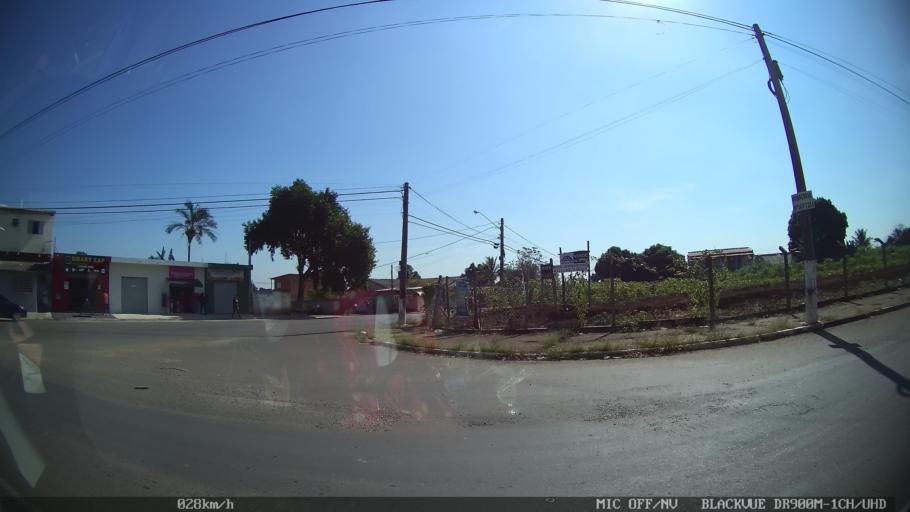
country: BR
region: Sao Paulo
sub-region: Indaiatuba
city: Indaiatuba
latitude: -23.0338
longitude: -47.1050
